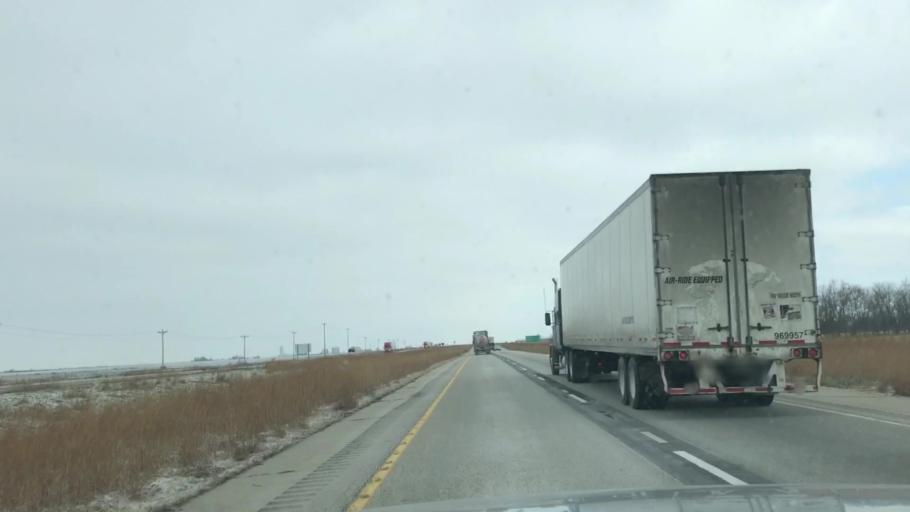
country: US
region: Illinois
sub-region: Sangamon County
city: Divernon
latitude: 39.4570
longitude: -89.6441
